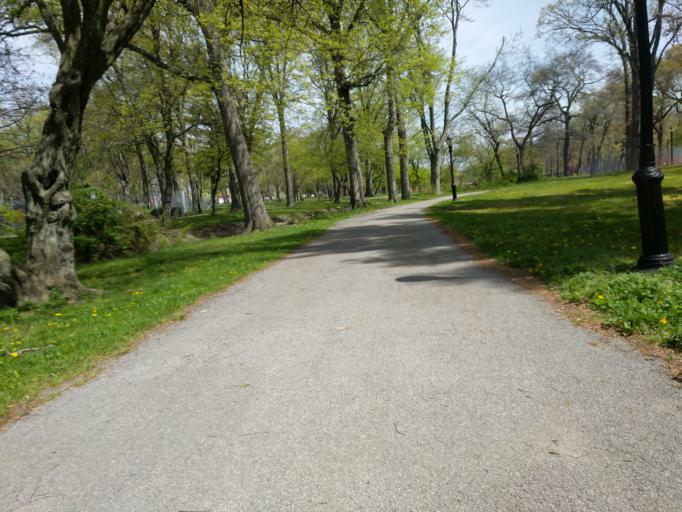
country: US
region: New York
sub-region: Nassau County
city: South Valley Stream
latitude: 40.6609
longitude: -73.7438
